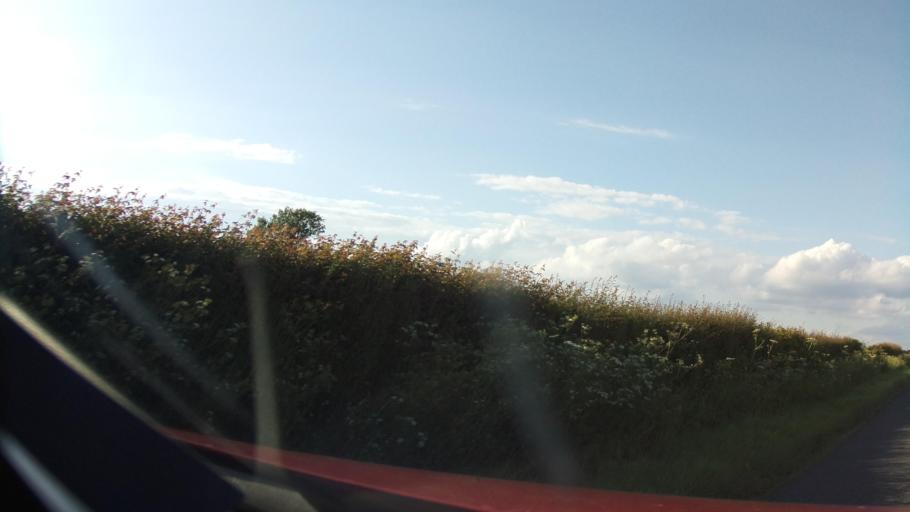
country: GB
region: England
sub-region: Lincolnshire
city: Navenby
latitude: 53.1039
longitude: -0.6075
